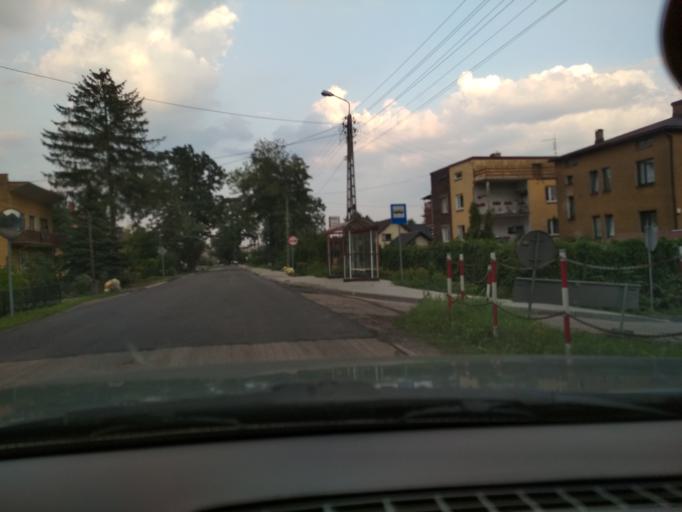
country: PL
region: Silesian Voivodeship
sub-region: Powiat cieszynski
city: Mnich
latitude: 49.8974
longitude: 18.7976
